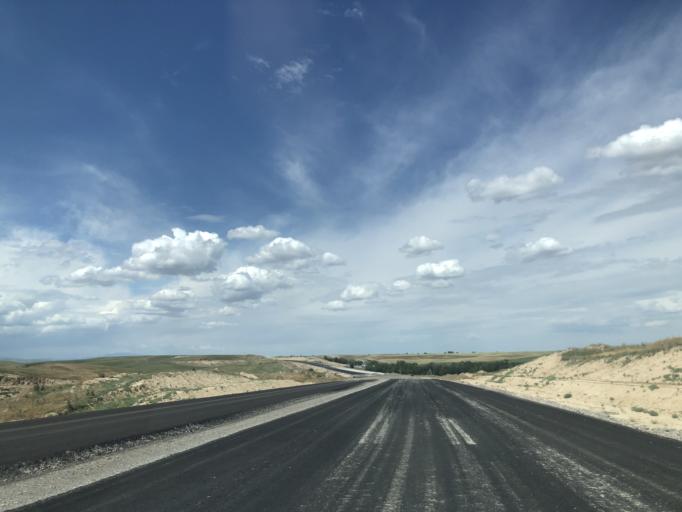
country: KG
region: Chuy
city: Bystrovka
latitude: 43.3194
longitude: 76.0693
